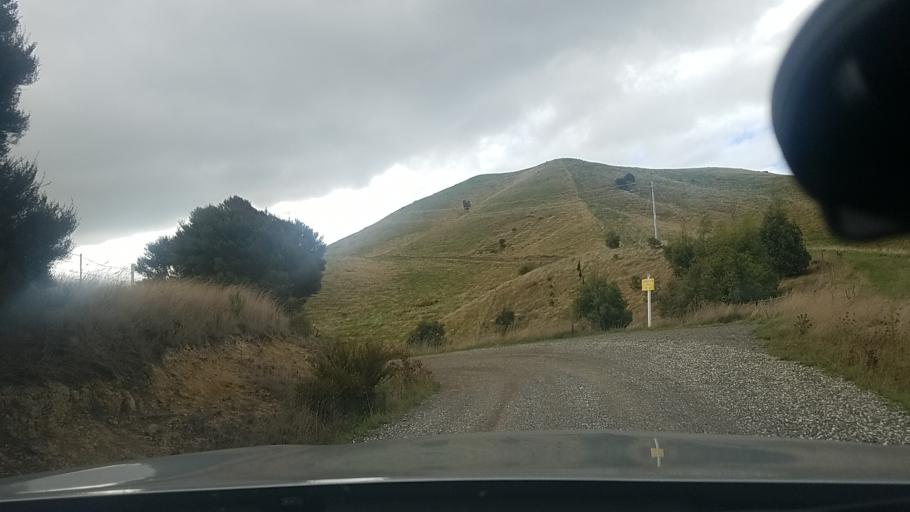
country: NZ
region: Marlborough
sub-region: Marlborough District
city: Blenheim
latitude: -41.5861
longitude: 174.0751
